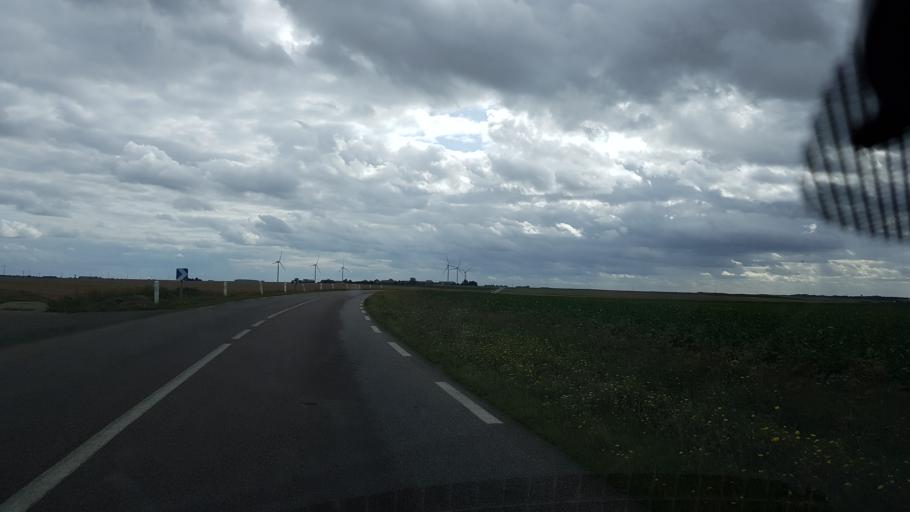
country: FR
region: Ile-de-France
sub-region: Departement de l'Essonne
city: Morigny-Champigny
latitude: 48.4125
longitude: 2.1791
